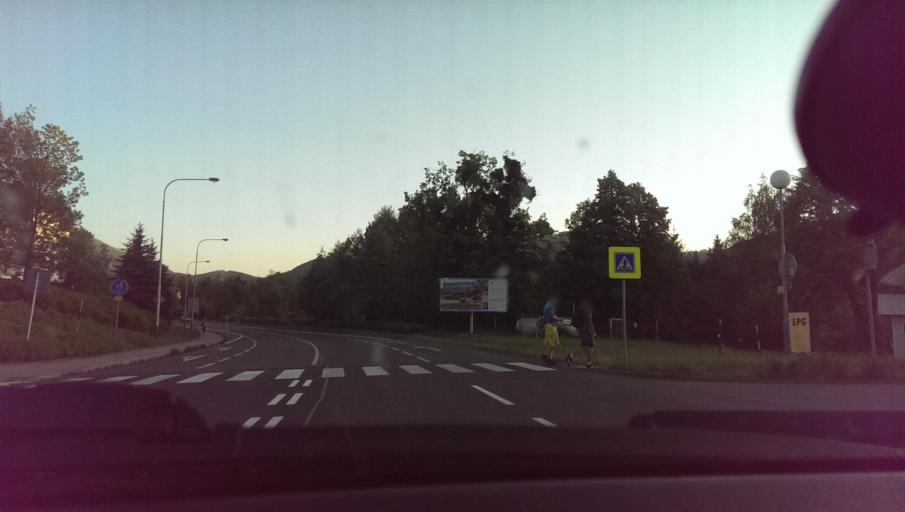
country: CZ
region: Moravskoslezsky
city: Frenstat pod Radhostem
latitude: 49.5397
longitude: 18.2052
